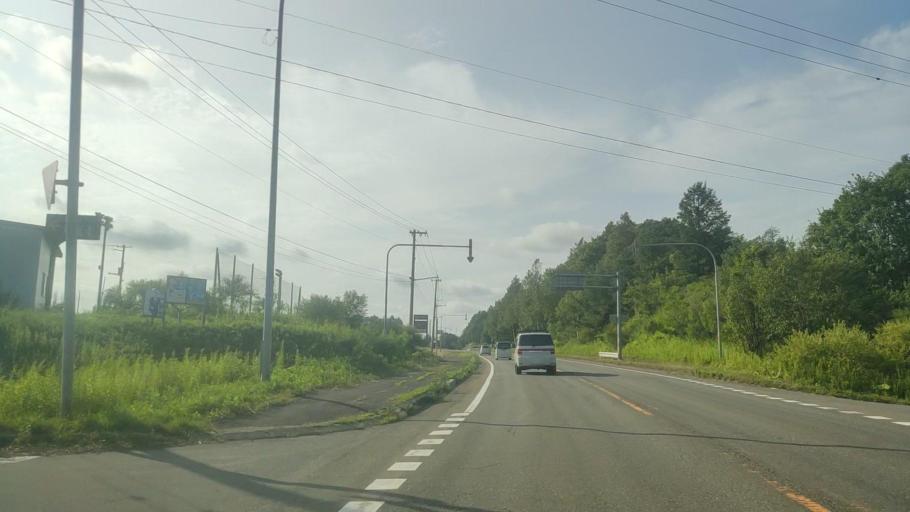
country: JP
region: Hokkaido
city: Chitose
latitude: 42.8747
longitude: 141.8212
